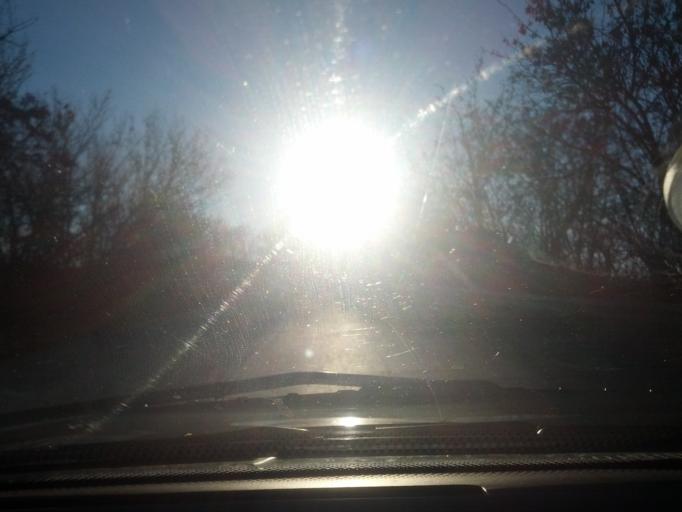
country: BG
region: Vratsa
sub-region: Obshtina Borovan
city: Borovan
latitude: 43.3704
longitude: 23.7022
